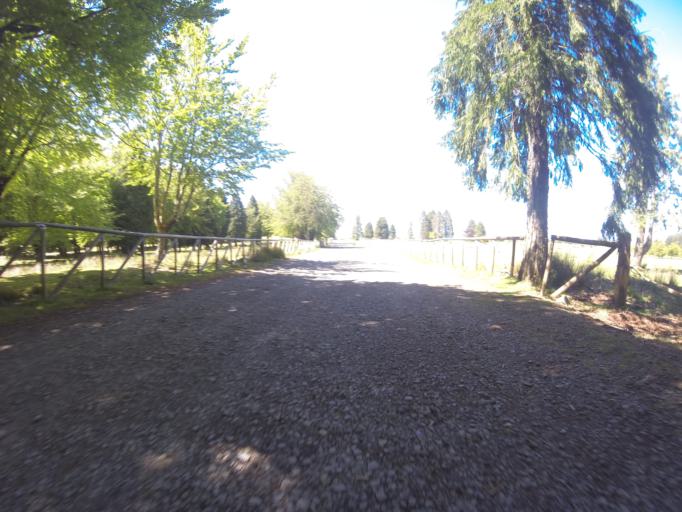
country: PT
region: Madeira
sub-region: Funchal
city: Nossa Senhora do Monte
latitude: 32.7240
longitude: -16.8866
